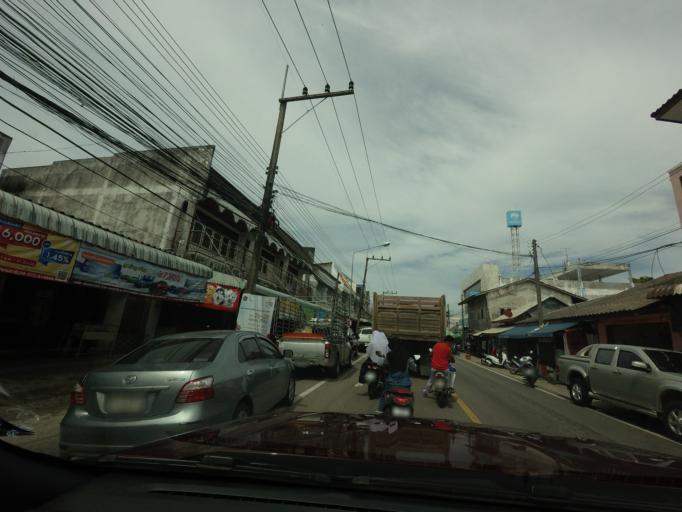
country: TH
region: Narathiwat
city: Tak Bai
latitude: 6.2591
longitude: 102.0529
